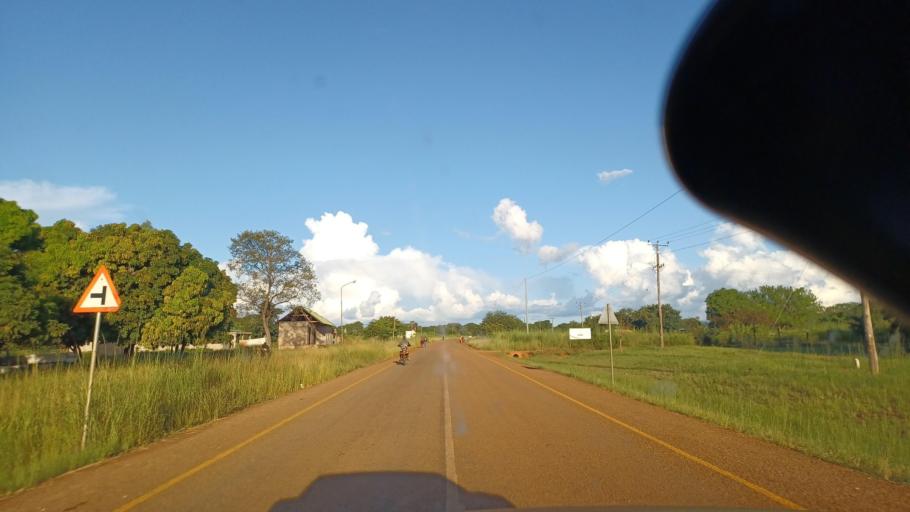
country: ZM
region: North-Western
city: Kalengwa
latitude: -13.1384
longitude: 25.0136
